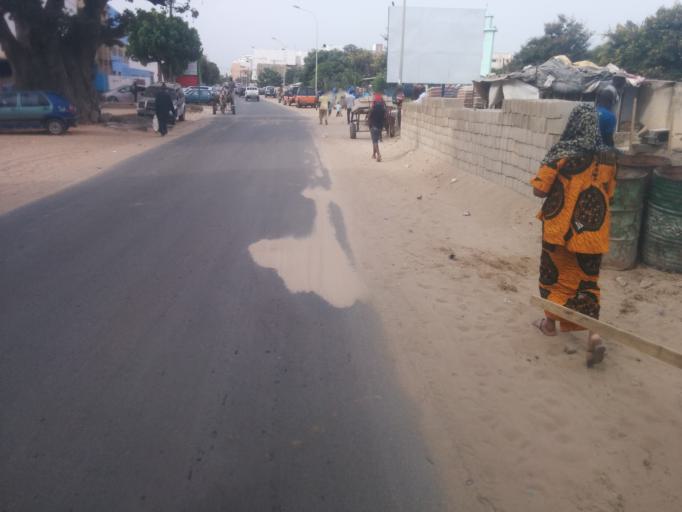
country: SN
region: Dakar
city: Grand Dakar
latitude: 14.7323
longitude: -17.4568
